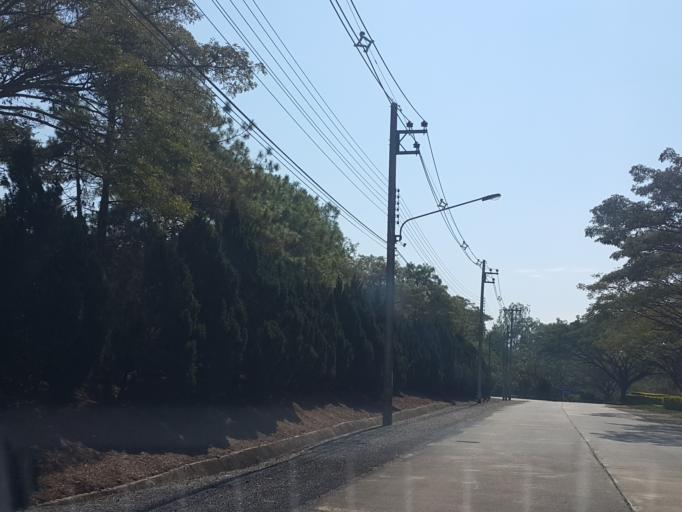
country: TH
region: Chiang Mai
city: Mae Taeng
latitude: 19.0237
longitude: 98.9895
